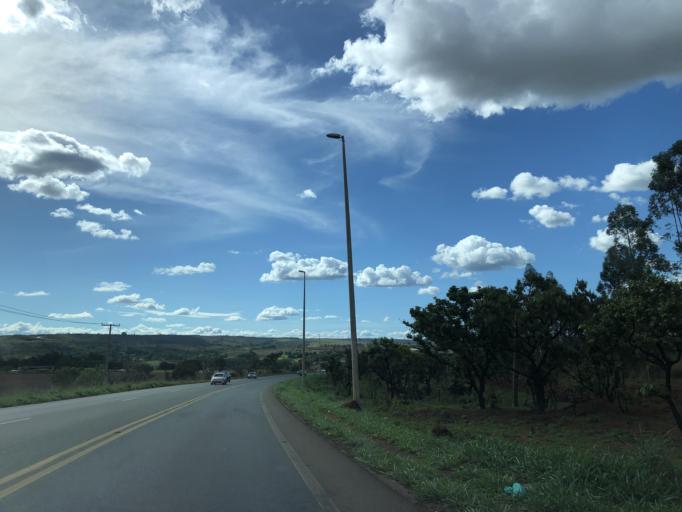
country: BR
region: Goias
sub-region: Luziania
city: Luziania
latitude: -16.0180
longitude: -48.1078
